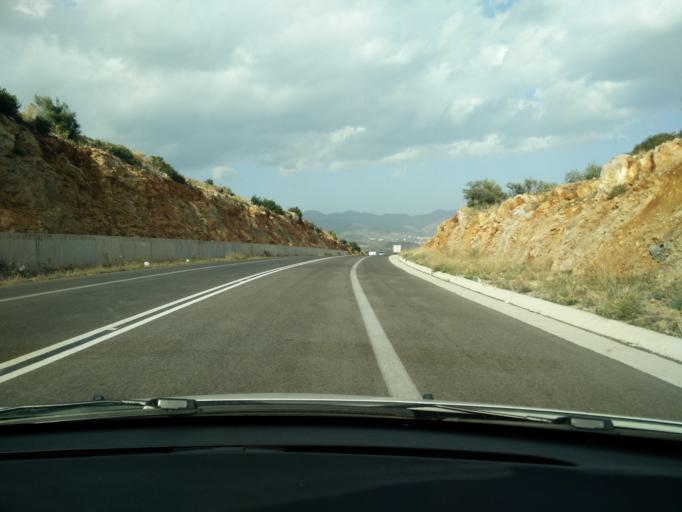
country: GR
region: Crete
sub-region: Nomos Lasithiou
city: Agios Nikolaos
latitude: 35.1734
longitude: 25.7009
